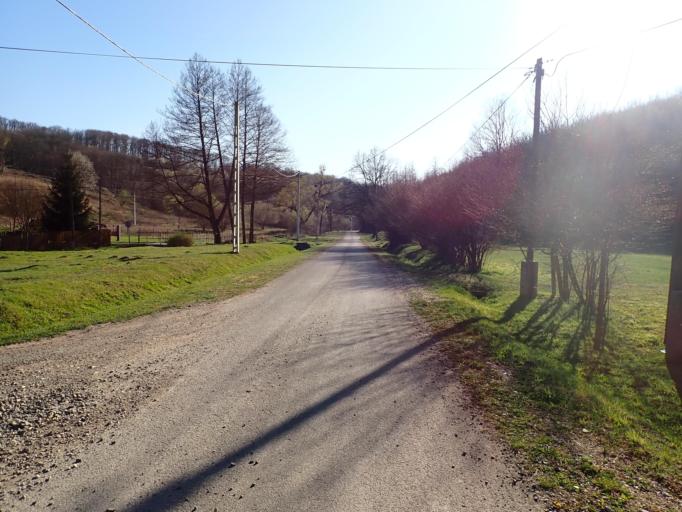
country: HU
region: Baranya
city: Komlo
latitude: 46.1637
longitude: 18.2589
